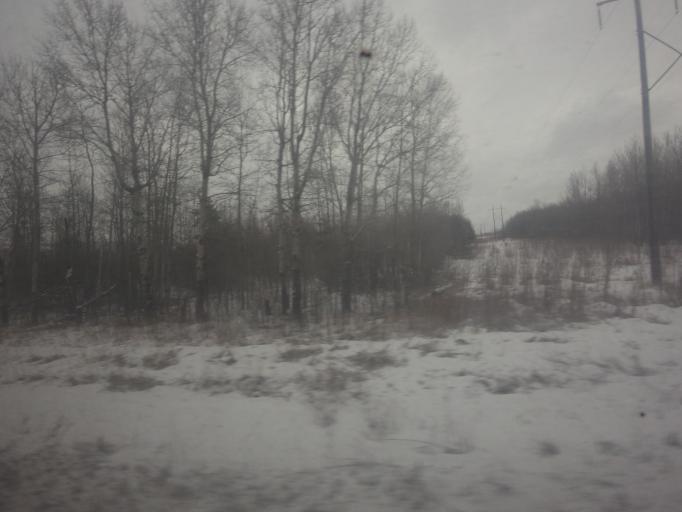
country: CA
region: Ontario
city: Bells Corners
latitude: 45.2424
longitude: -75.7984
